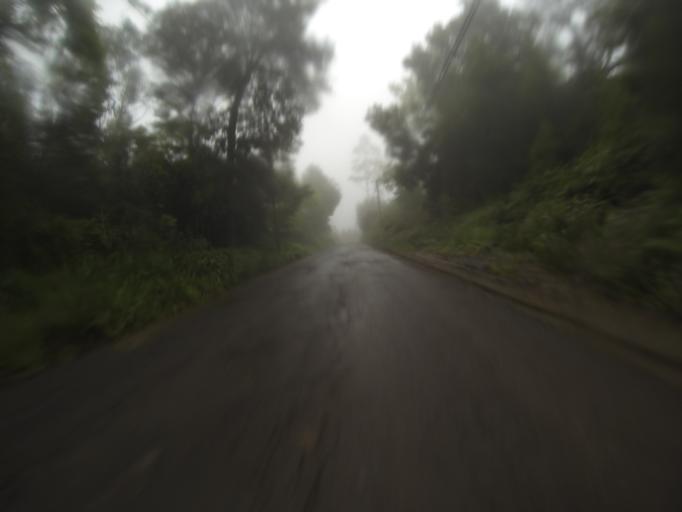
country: PT
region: Madeira
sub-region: Santa Cruz
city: Camacha
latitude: 32.6767
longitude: -16.8667
